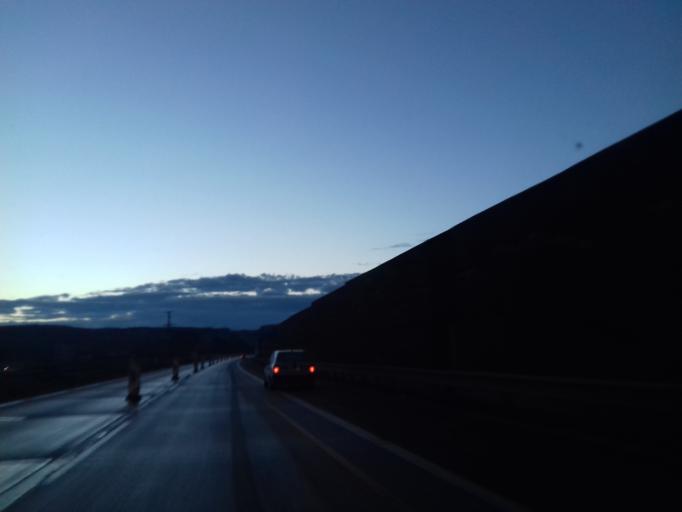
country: CZ
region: South Moravian
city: Ricany
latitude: 49.2184
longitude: 16.4062
